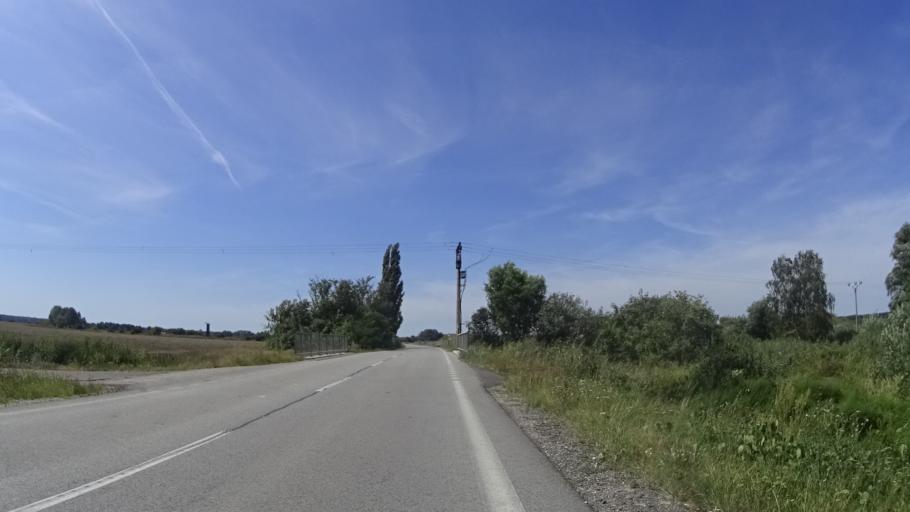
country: AT
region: Lower Austria
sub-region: Politischer Bezirk Ganserndorf
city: Marchegg
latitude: 48.3052
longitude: 16.9631
